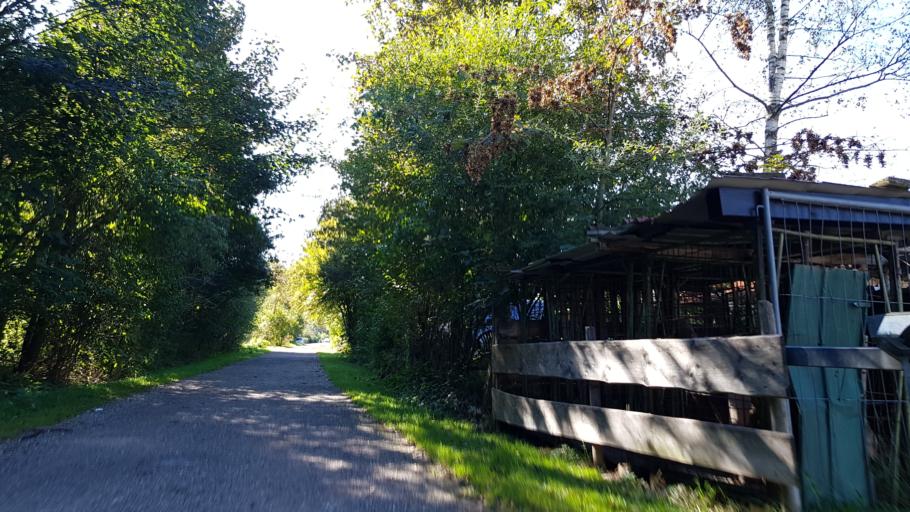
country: DE
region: Bavaria
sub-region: Swabia
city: Fuessen
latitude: 47.5840
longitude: 10.6793
